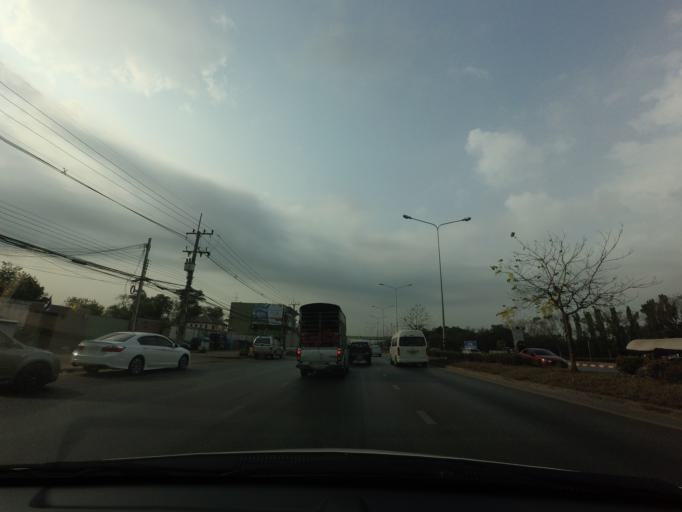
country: TH
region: Bangkok
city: Thawi Watthana
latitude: 13.7711
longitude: 100.3284
